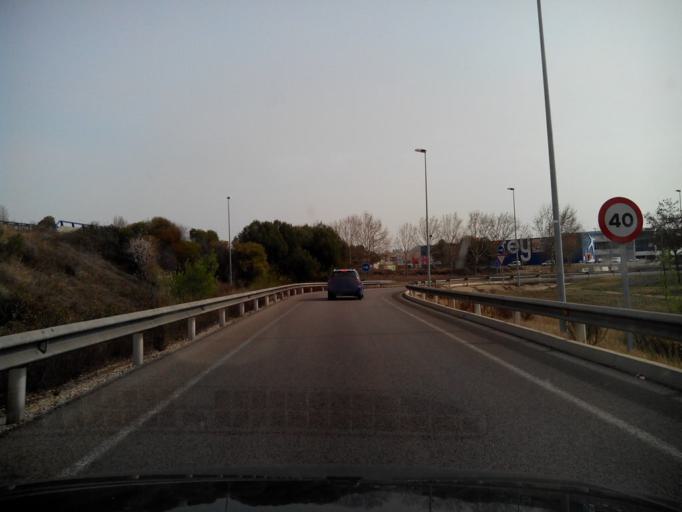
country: ES
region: Catalonia
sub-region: Provincia de Barcelona
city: Vilafranca del Penedes
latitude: 41.3342
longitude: 1.6814
